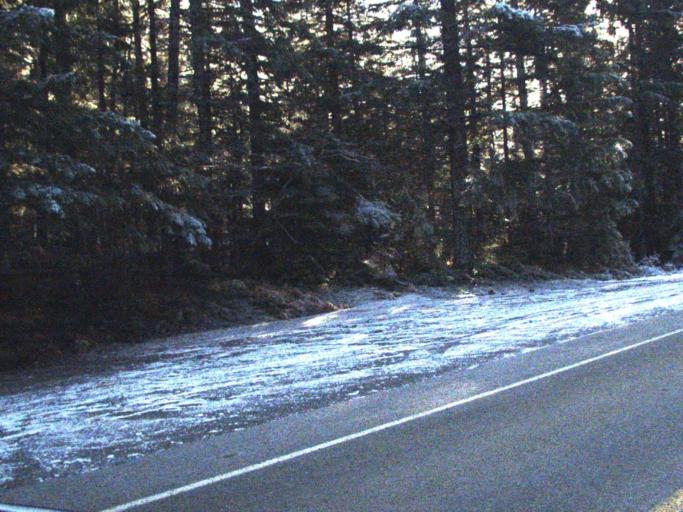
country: US
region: Washington
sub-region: Snohomish County
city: Darrington
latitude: 48.7005
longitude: -121.1104
